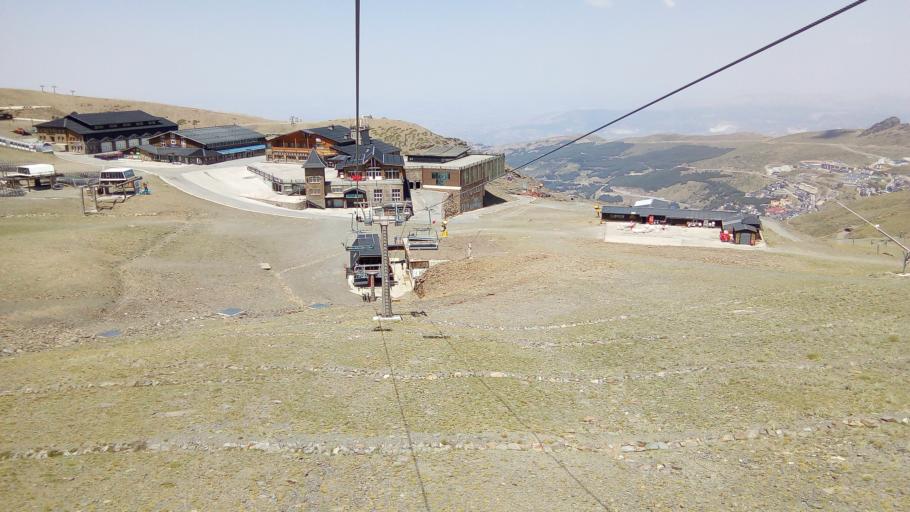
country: ES
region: Andalusia
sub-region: Provincia de Granada
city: Guejar-Sierra
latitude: 37.0701
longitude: -3.3858
